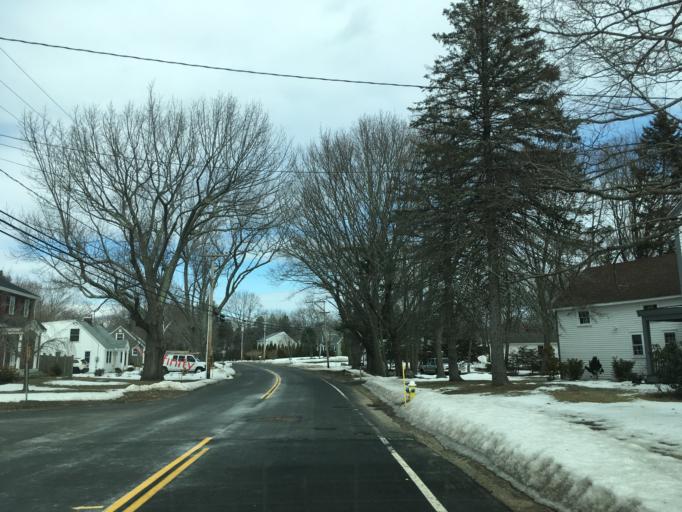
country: US
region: New Hampshire
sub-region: Rockingham County
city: Hampton
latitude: 42.9347
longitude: -70.8200
